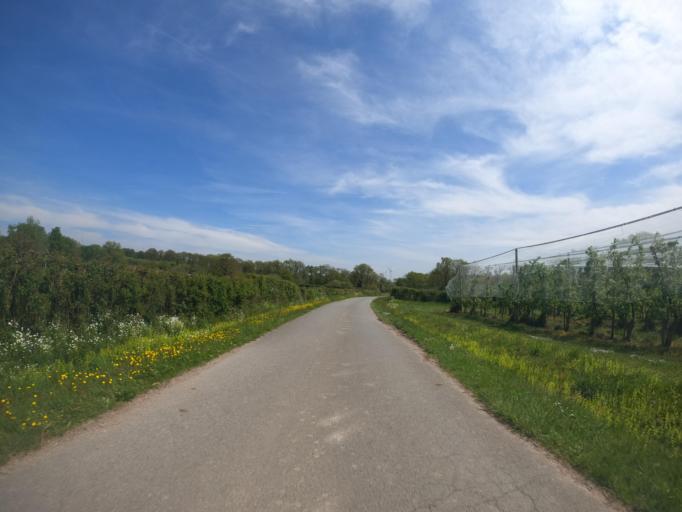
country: FR
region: Poitou-Charentes
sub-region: Departement des Deux-Sevres
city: Secondigny
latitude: 46.6520
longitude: -0.5021
